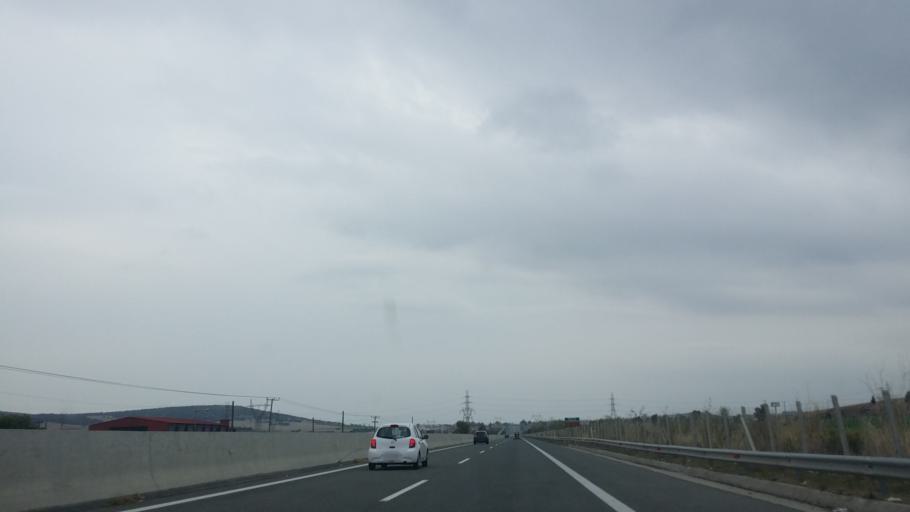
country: GR
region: Central Greece
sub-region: Nomos Voiotias
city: Arma
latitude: 38.3770
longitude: 23.4577
